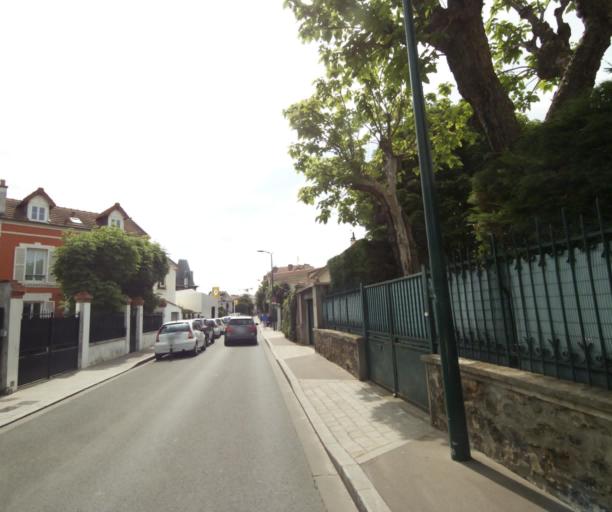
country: FR
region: Ile-de-France
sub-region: Departement des Hauts-de-Seine
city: Bois-Colombes
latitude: 48.9266
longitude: 2.2643
